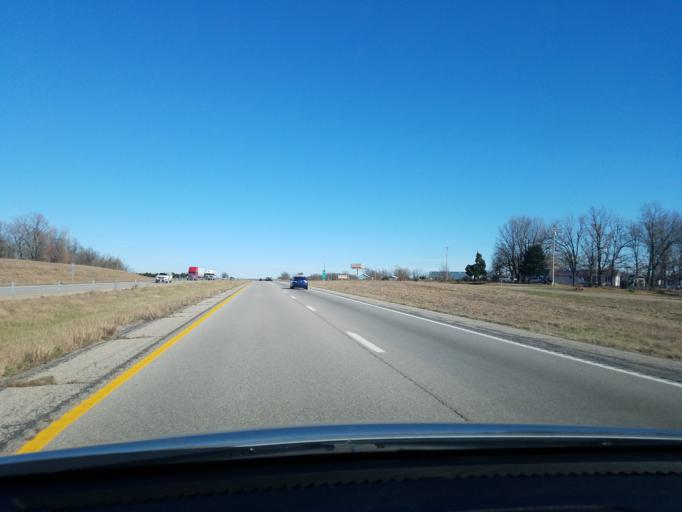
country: US
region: Missouri
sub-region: Laclede County
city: Lebanon
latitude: 37.5918
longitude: -92.7294
